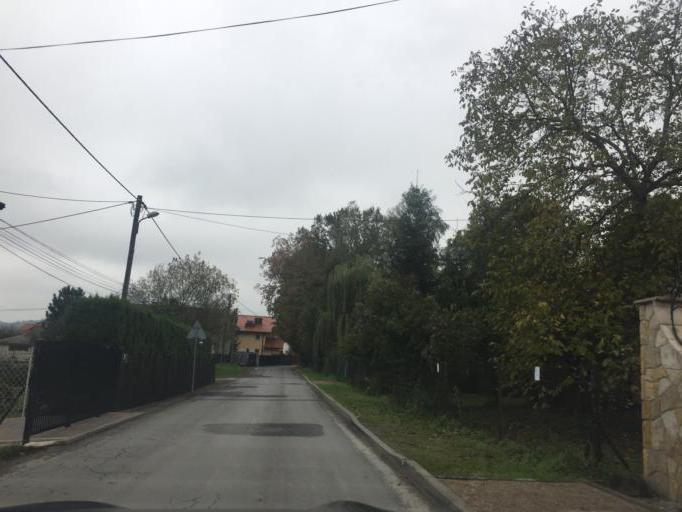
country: PL
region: Lesser Poland Voivodeship
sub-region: Powiat wielicki
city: Wieliczka
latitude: 49.9948
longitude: 20.0248
